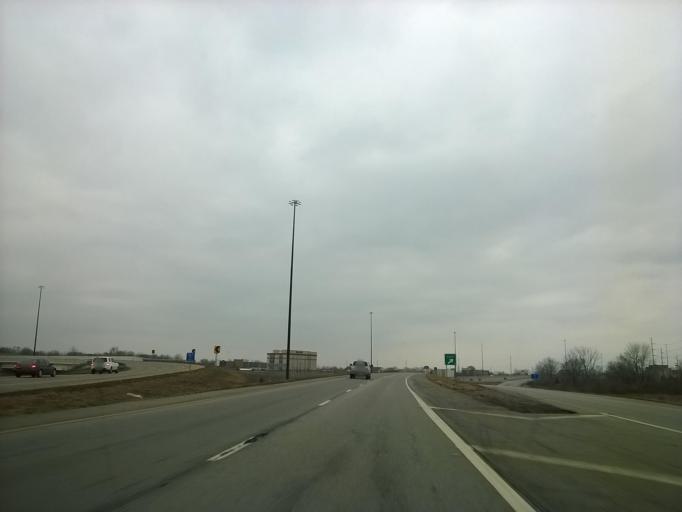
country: US
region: Indiana
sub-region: Marion County
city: Warren Park
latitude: 39.8005
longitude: -86.0361
